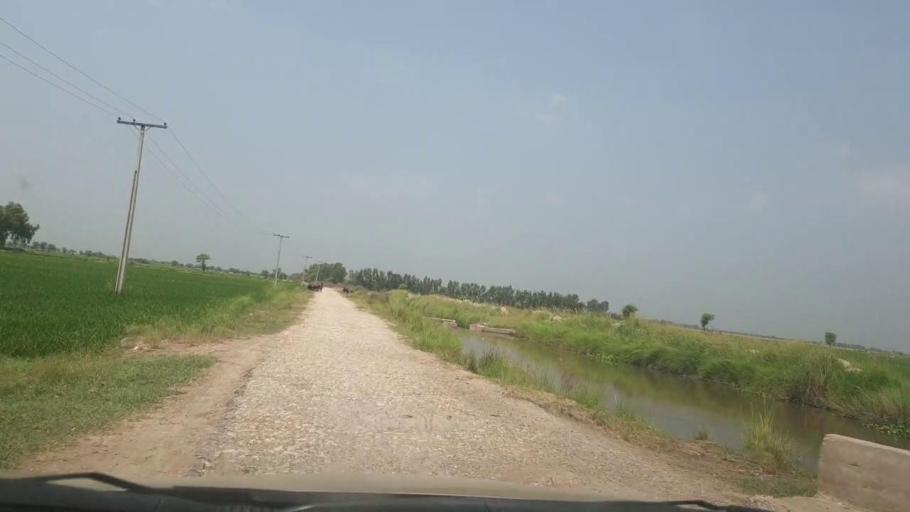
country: PK
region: Sindh
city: Ratodero
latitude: 27.6890
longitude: 68.2360
